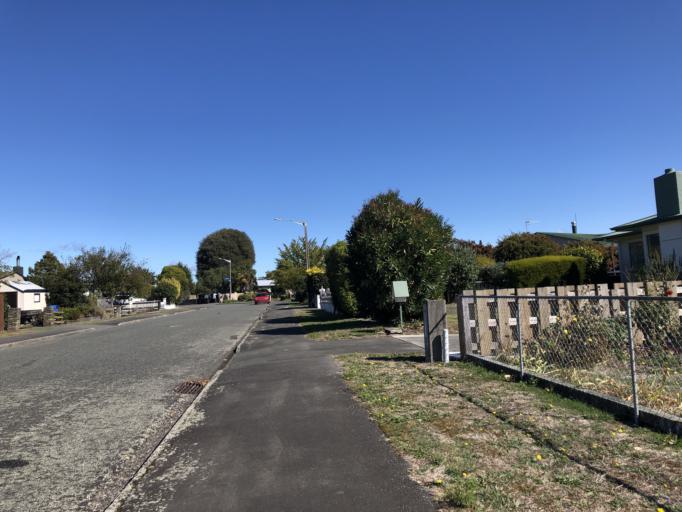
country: NZ
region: Tasman
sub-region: Tasman District
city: Richmond
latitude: -41.3416
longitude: 173.1758
